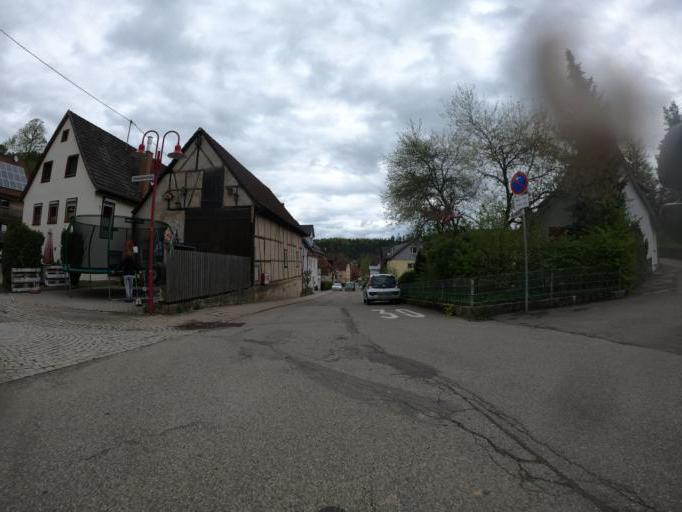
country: DE
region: Baden-Wuerttemberg
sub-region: Karlsruhe Region
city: Nagold
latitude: 48.5165
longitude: 8.7063
